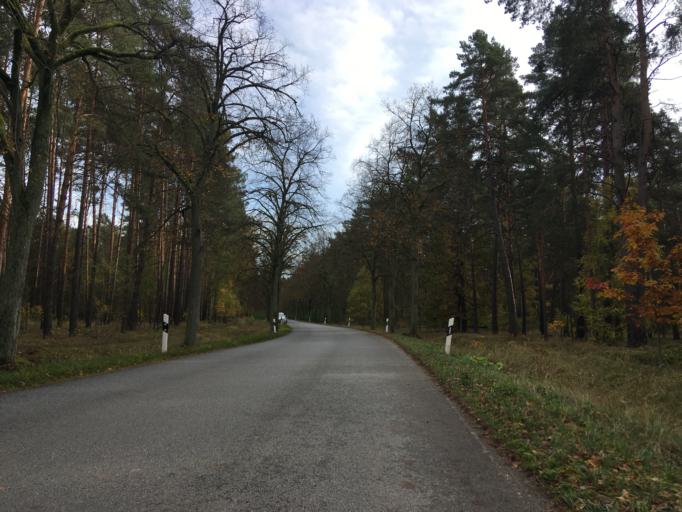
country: DE
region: Brandenburg
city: Marienwerder
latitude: 52.9219
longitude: 13.5112
